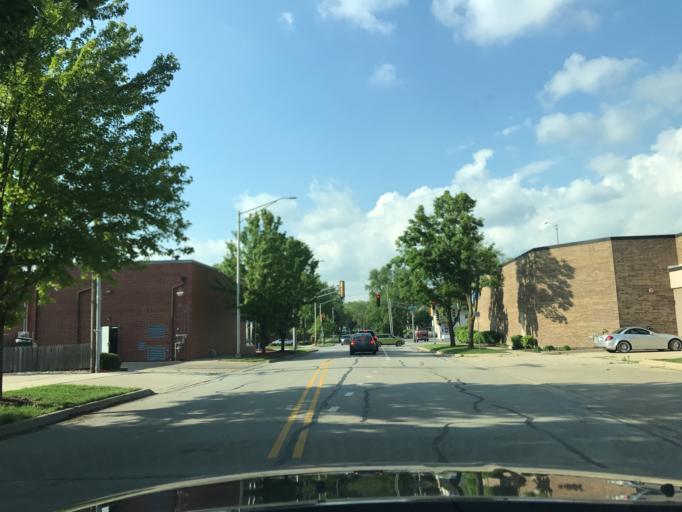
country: US
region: Illinois
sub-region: DuPage County
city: Naperville
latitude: 41.7849
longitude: -88.1414
